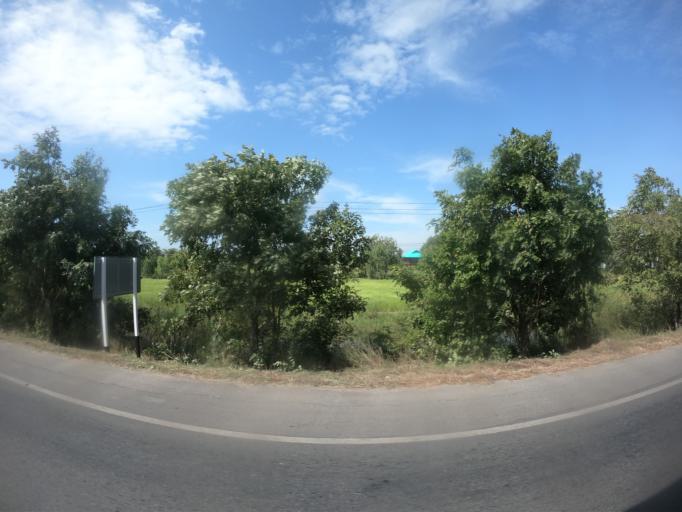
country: TH
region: Khon Kaen
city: Khon Kaen
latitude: 16.4320
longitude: 102.9175
